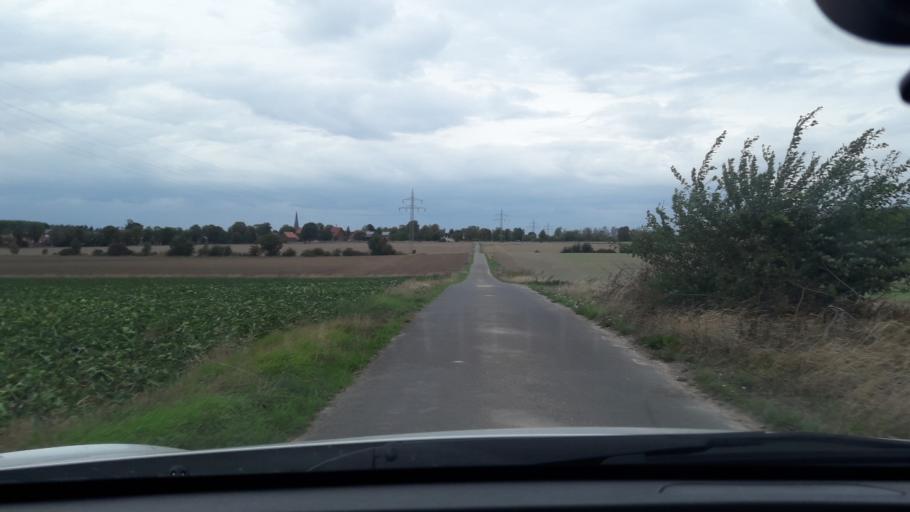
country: DE
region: Lower Saxony
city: Flothe
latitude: 52.0552
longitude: 10.4547
